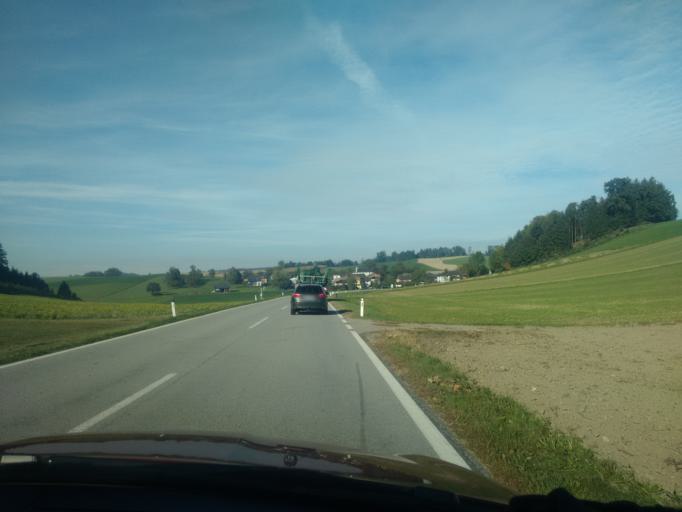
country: AT
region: Upper Austria
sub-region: Politischer Bezirk Vocklabruck
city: Rutzenham
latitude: 48.0609
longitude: 13.7243
